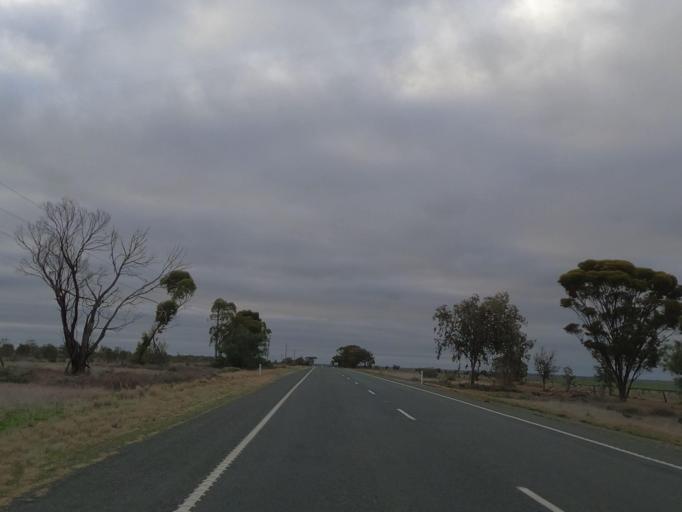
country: AU
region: Victoria
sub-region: Swan Hill
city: Swan Hill
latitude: -35.5711
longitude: 143.7861
